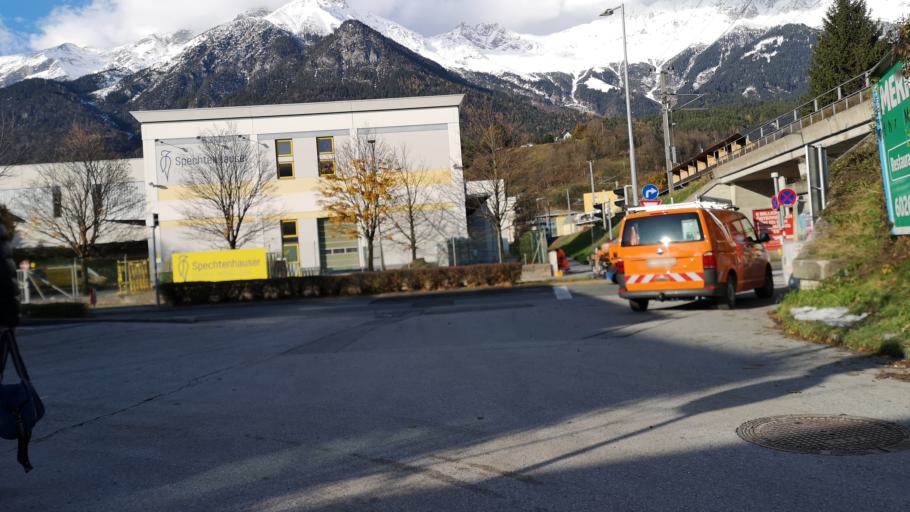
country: AT
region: Tyrol
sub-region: Innsbruck Stadt
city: Innsbruck
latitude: 47.2624
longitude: 11.3732
